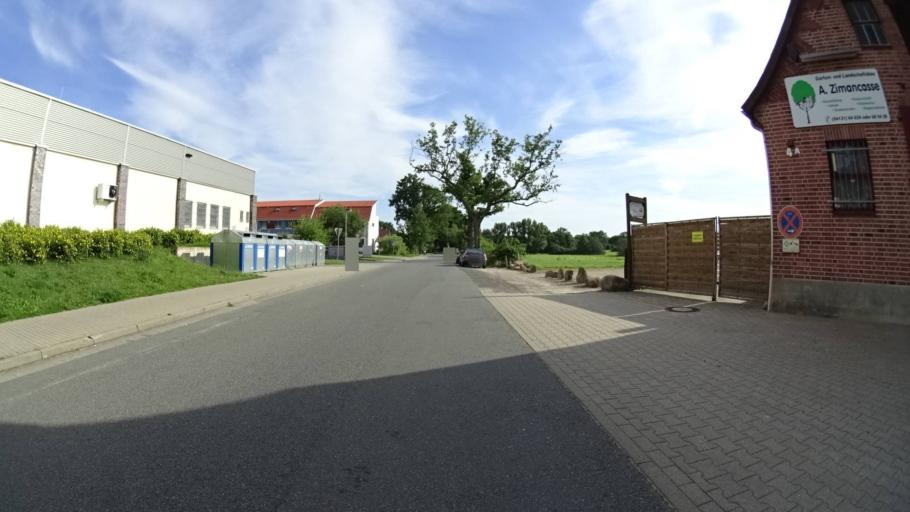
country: DE
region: Lower Saxony
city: Reppenstedt
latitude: 53.2468
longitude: 10.3593
